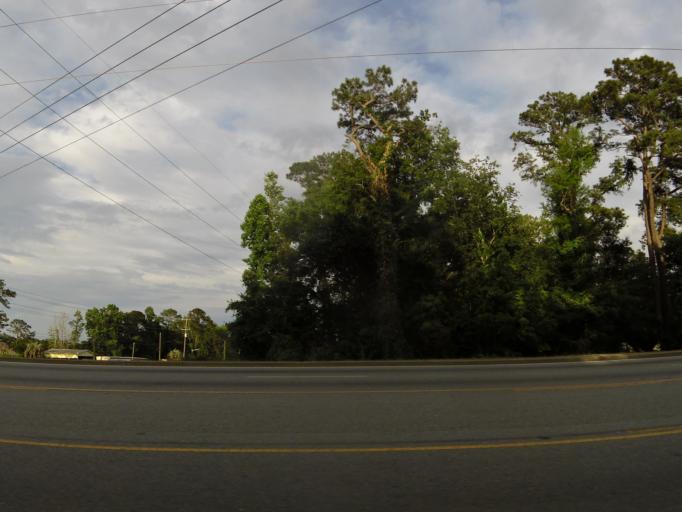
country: US
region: Georgia
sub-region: Chatham County
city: Garden City
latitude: 32.0821
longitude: -81.1956
